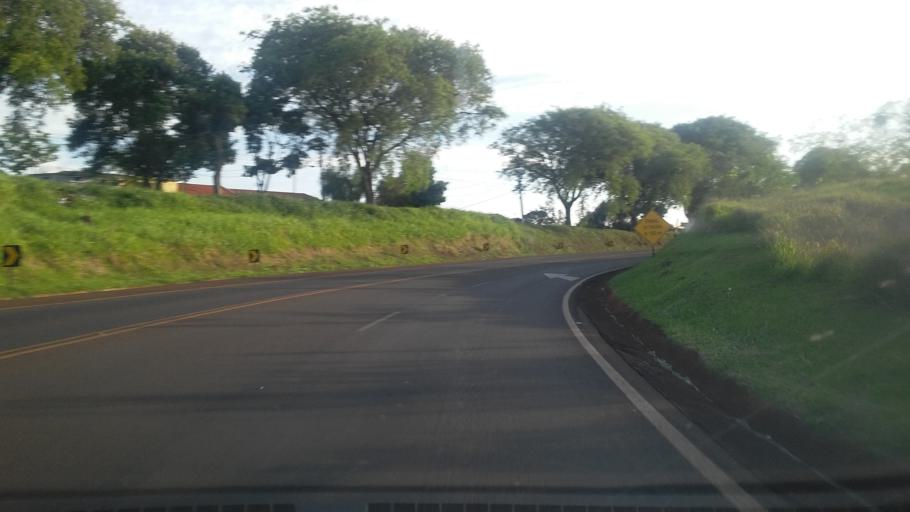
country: BR
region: Parana
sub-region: Bandeirantes
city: Bandeirantes
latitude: -23.1746
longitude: -50.6236
